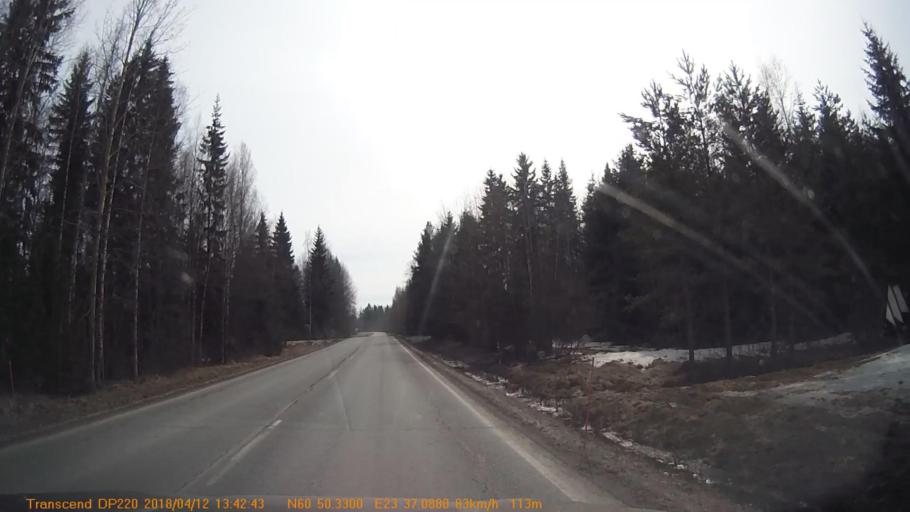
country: FI
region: Haeme
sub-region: Forssa
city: Forssa
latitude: 60.8382
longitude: 23.6181
